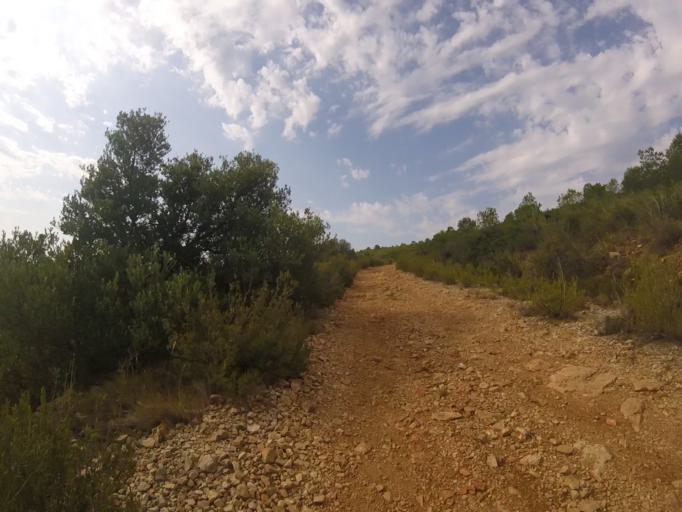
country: ES
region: Valencia
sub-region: Provincia de Castello
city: Alcala de Xivert
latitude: 40.3866
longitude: 0.2116
